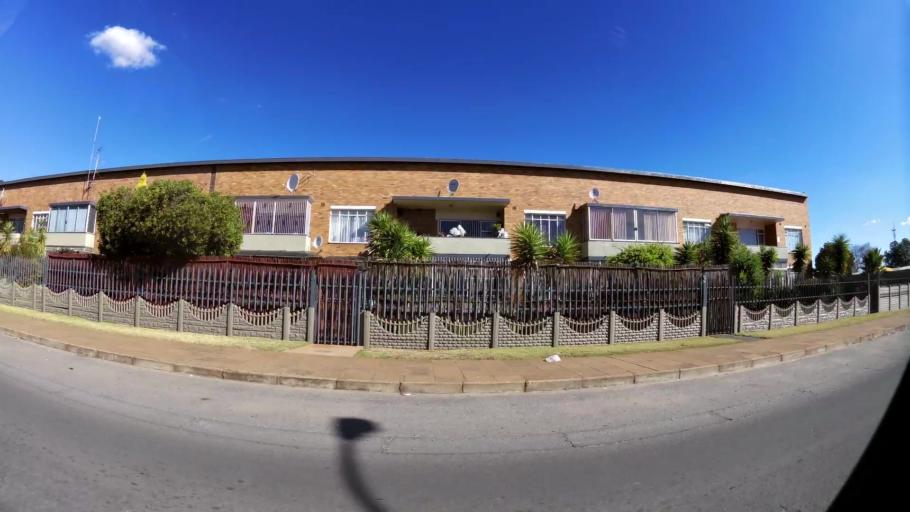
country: ZA
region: Gauteng
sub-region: West Rand District Municipality
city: Carletonville
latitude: -26.3571
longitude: 27.3927
